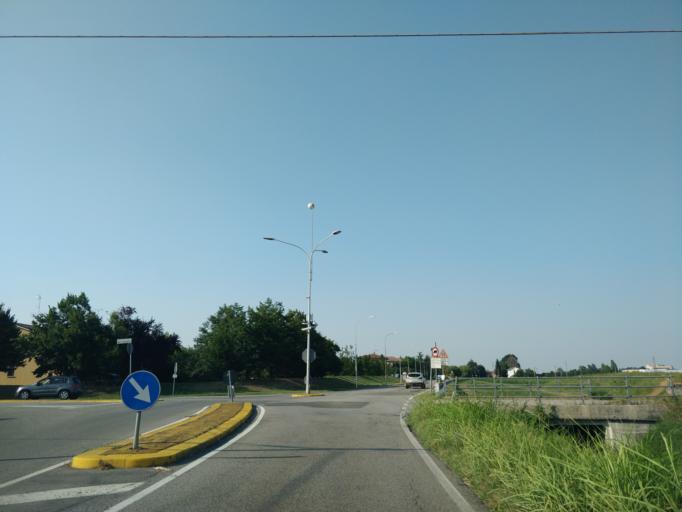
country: IT
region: Emilia-Romagna
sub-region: Provincia di Bologna
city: Argelato
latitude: 44.6352
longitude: 11.3446
